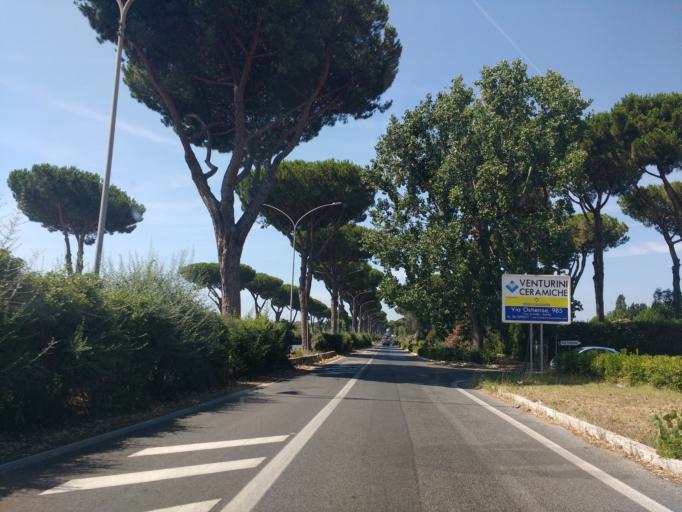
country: IT
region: Latium
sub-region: Citta metropolitana di Roma Capitale
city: Acilia-Castel Fusano-Ostia Antica
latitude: 41.7399
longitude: 12.3500
